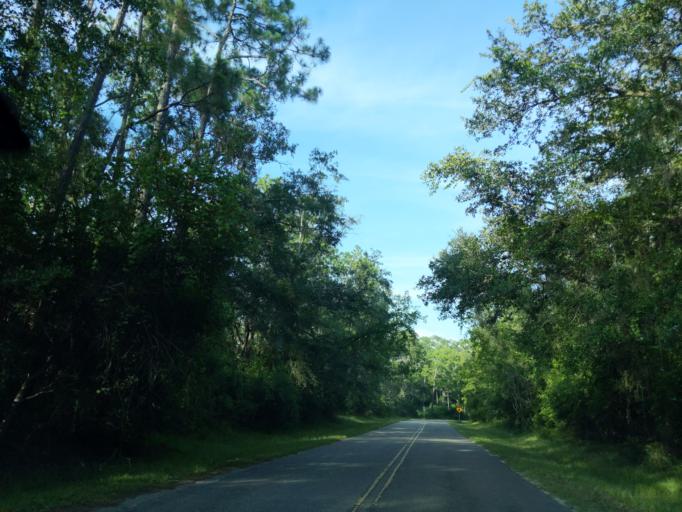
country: US
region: Florida
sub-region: Leon County
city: Tallahassee
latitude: 30.3445
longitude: -84.3866
